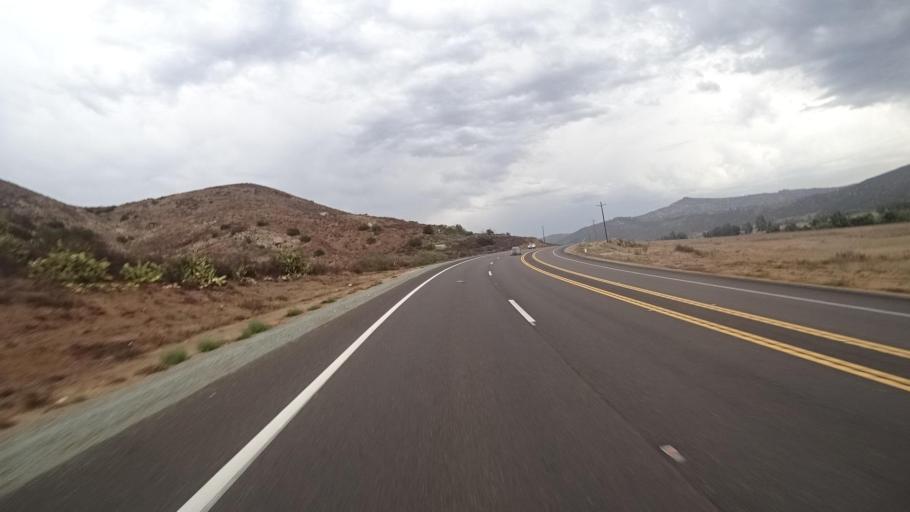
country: US
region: California
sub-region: San Diego County
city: San Pasqual
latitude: 33.0985
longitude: -117.0142
